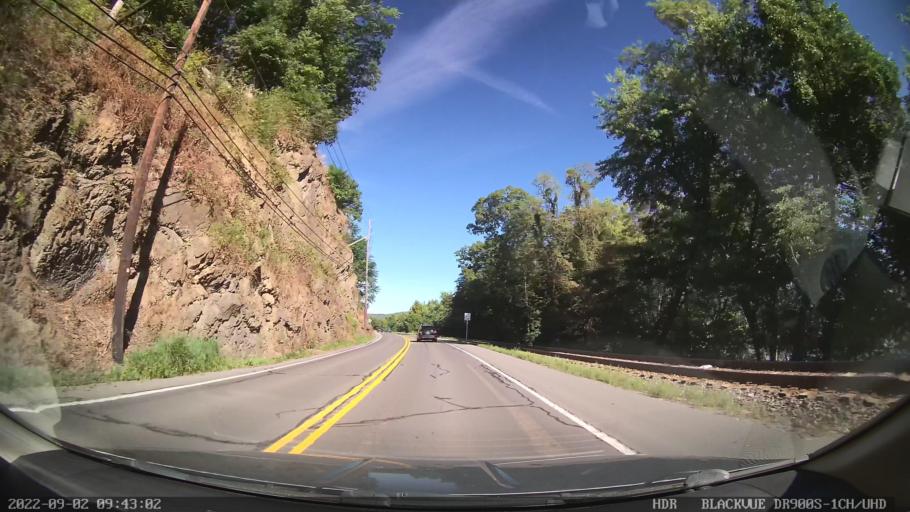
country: US
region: Pennsylvania
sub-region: Montour County
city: Danville
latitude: 40.9505
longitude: -76.6154
